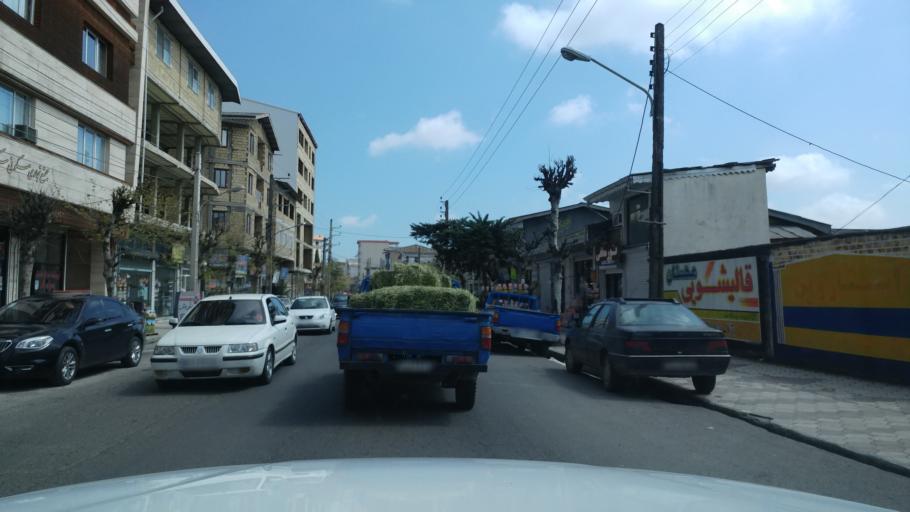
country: IR
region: Gilan
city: Hashtpar
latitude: 37.7933
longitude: 48.9051
